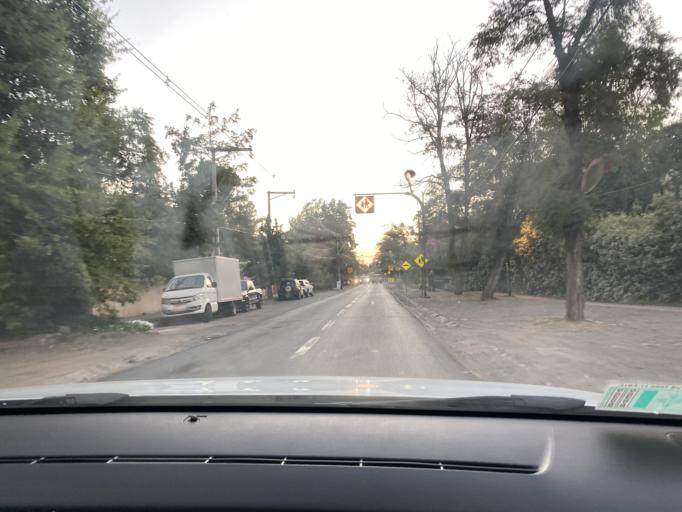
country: CL
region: Santiago Metropolitan
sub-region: Provincia de Santiago
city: Villa Presidente Frei, Nunoa, Santiago, Chile
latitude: -33.3619
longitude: -70.4834
